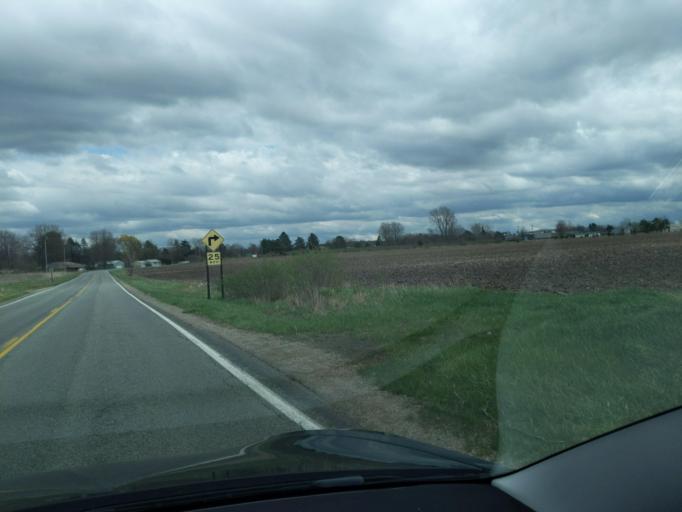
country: US
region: Michigan
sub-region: Ingham County
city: Mason
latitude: 42.5662
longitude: -84.4579
